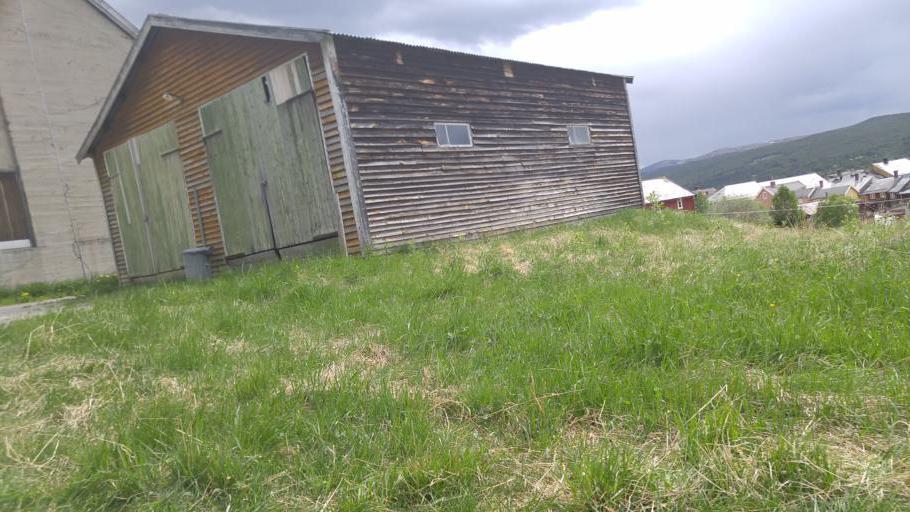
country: NO
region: Sor-Trondelag
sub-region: Roros
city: Roros
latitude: 62.5768
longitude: 11.3847
